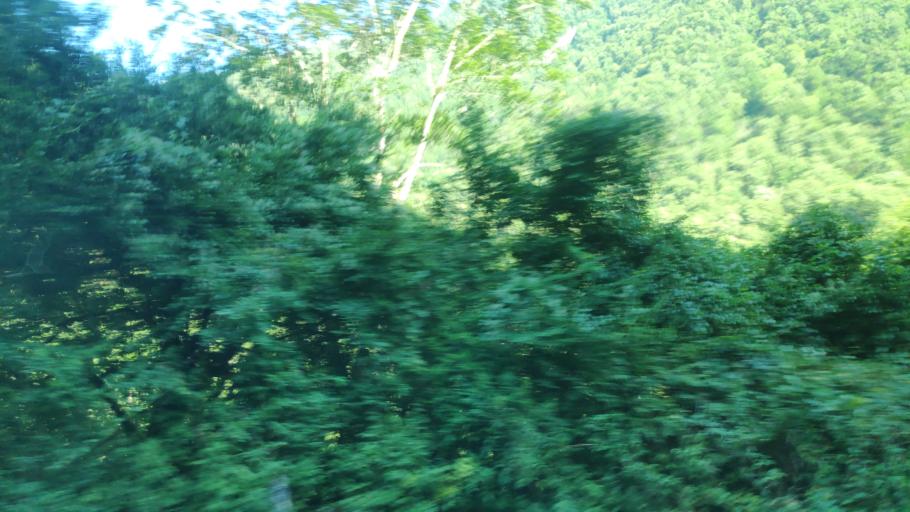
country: GE
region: Abkhazia
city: Gagra
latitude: 43.3545
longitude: 40.4212
